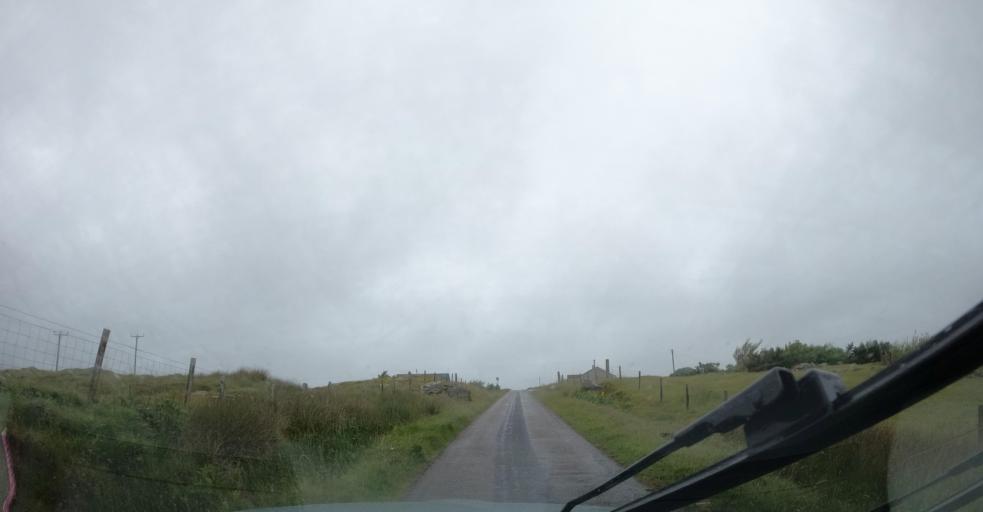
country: GB
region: Scotland
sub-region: Eilean Siar
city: Benbecula
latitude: 57.4992
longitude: -7.2531
